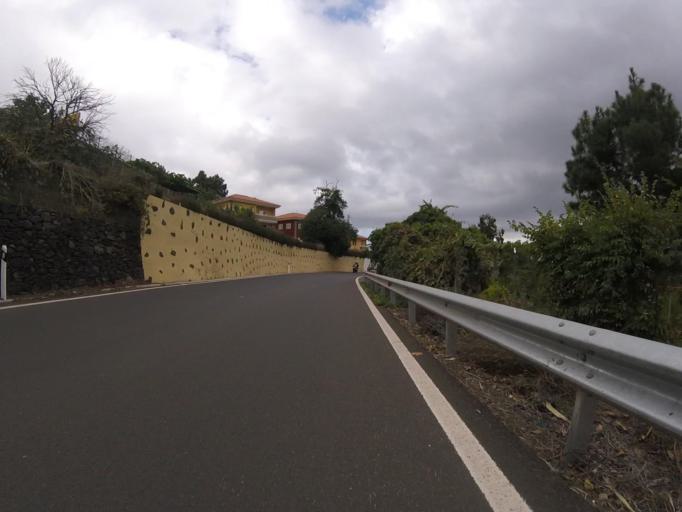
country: ES
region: Canary Islands
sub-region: Provincia de Las Palmas
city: Vega de San Mateo
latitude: 28.0064
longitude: -15.5526
